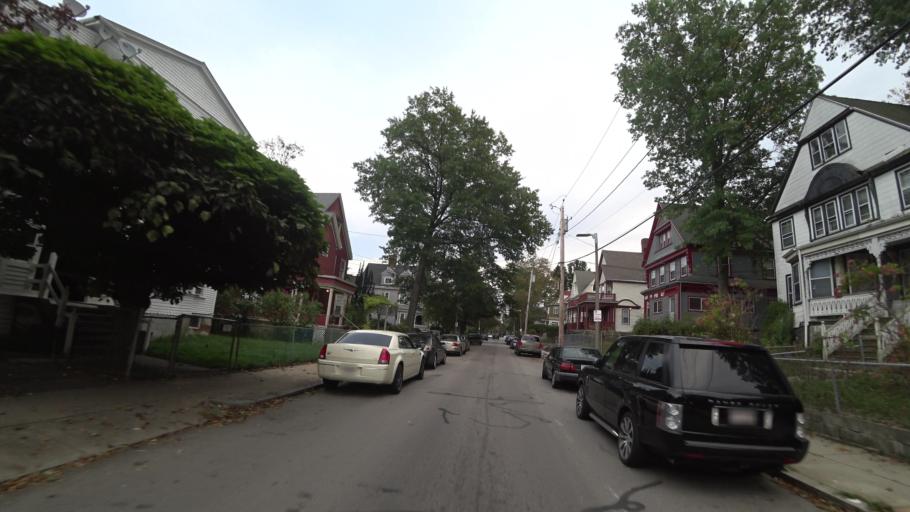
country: US
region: Massachusetts
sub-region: Suffolk County
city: Jamaica Plain
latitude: 42.3128
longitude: -71.0882
